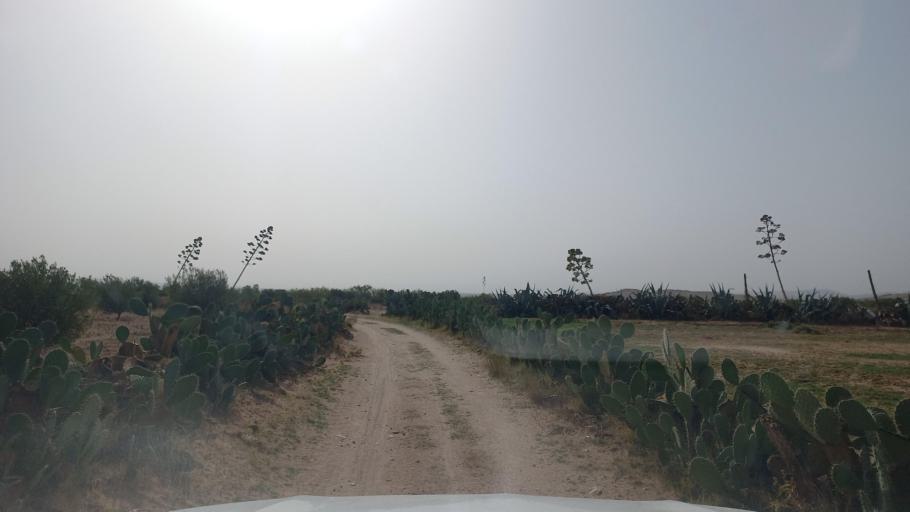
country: TN
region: Al Qasrayn
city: Kasserine
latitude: 35.2965
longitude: 8.9624
